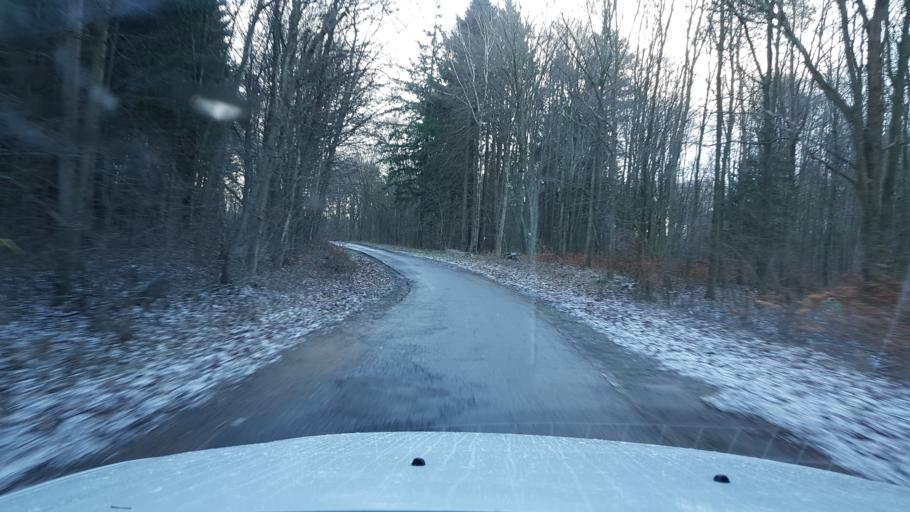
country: PL
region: West Pomeranian Voivodeship
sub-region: Powiat gryficki
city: Trzebiatow
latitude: 54.0472
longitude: 15.3217
